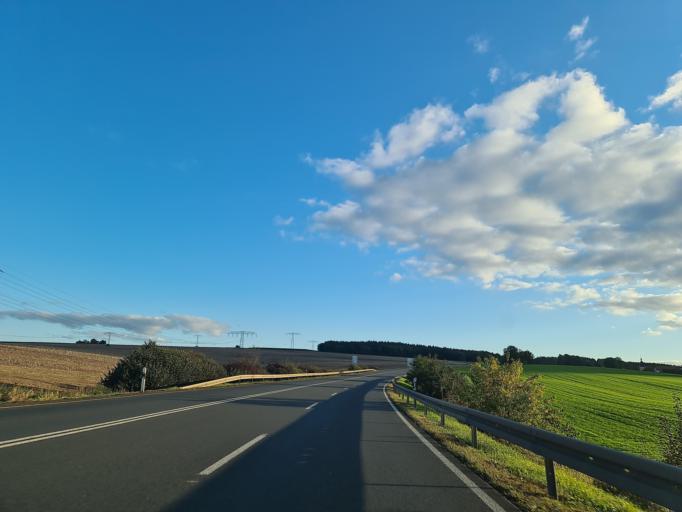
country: DE
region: Thuringia
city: Teichwitz
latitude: 50.7654
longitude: 12.0890
